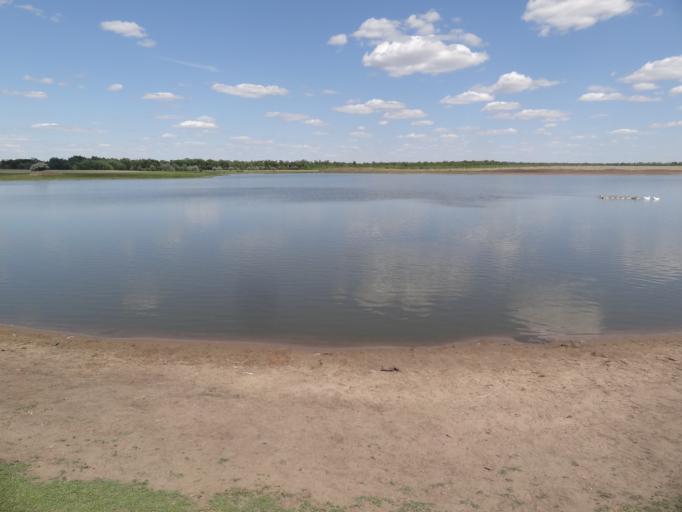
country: RU
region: Saratov
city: Sovetskoye
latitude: 51.2887
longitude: 46.6520
